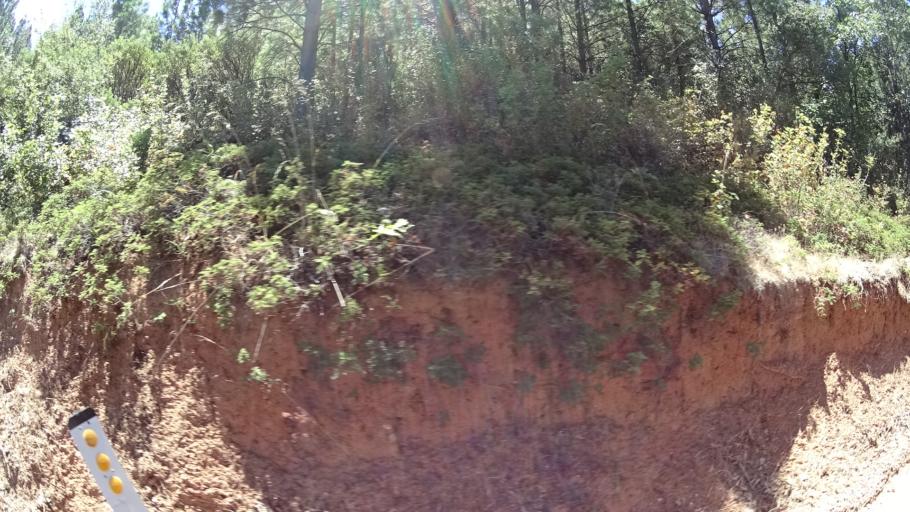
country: US
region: California
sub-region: Calaveras County
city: Forest Meadows
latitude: 38.1922
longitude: -120.4408
